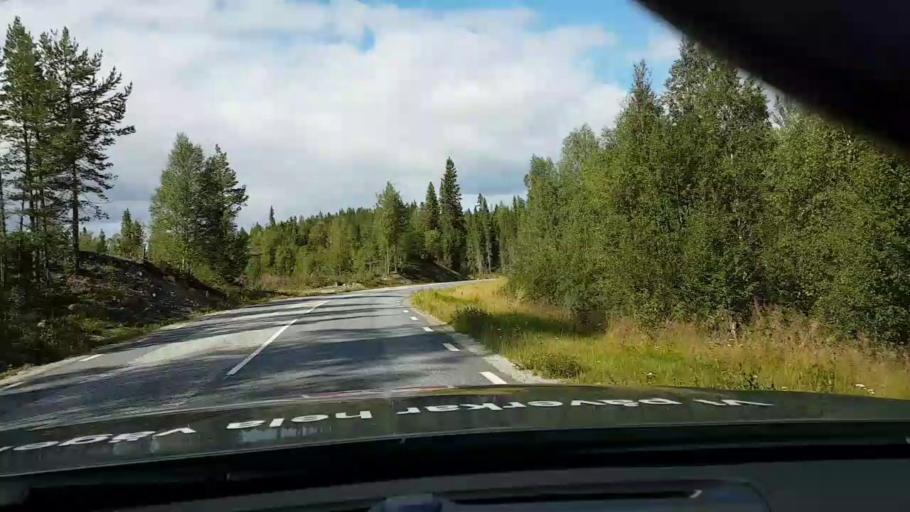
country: SE
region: Vaesterbotten
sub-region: Asele Kommun
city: Asele
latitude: 63.8432
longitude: 17.4236
